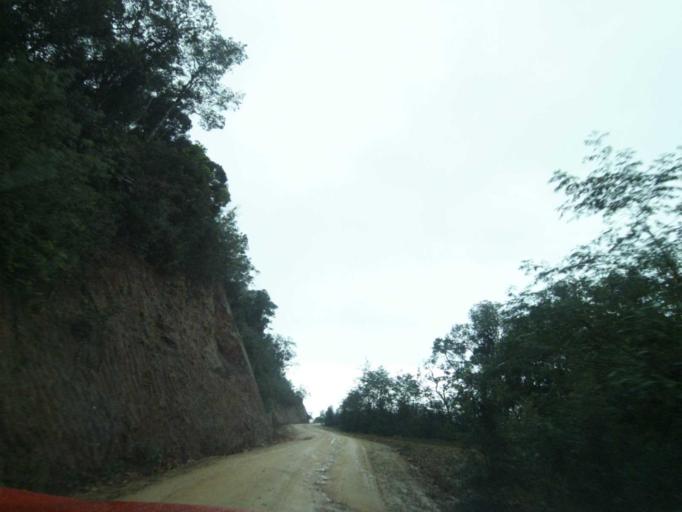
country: BR
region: Santa Catarina
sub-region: Anitapolis
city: Anitapolis
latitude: -27.9197
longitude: -49.1900
